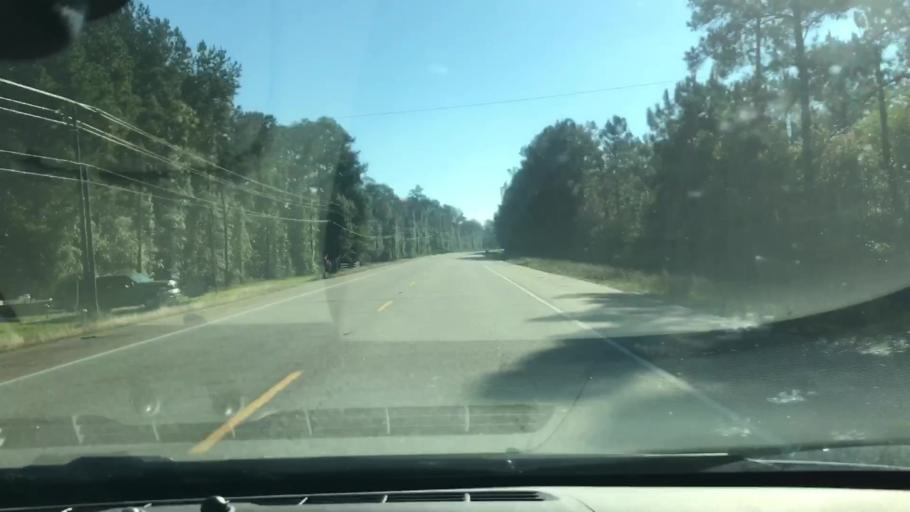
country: US
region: Mississippi
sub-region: Pearl River County
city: Nicholson
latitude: 30.5196
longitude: -89.8394
